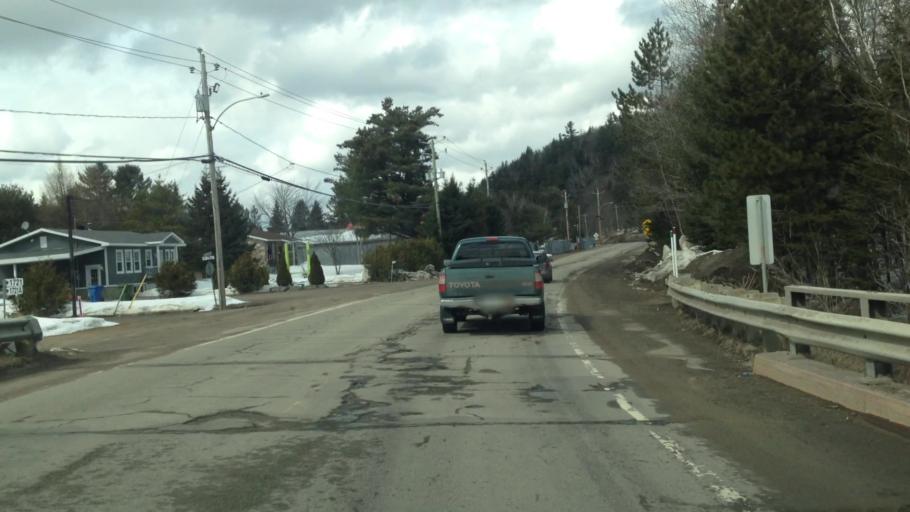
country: CA
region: Quebec
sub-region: Laurentides
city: Brownsburg-Chatham
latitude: 45.7292
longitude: -74.4851
